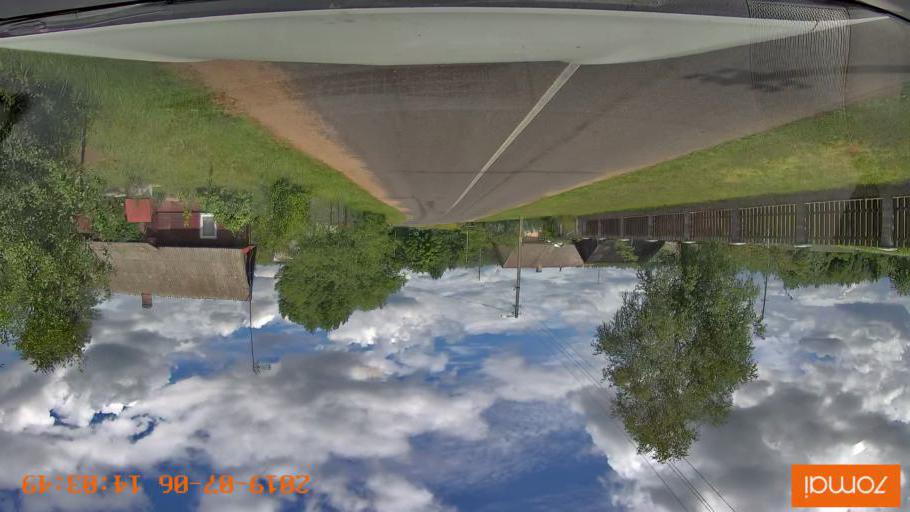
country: BY
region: Minsk
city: Ivyanyets
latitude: 53.8336
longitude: 26.8004
